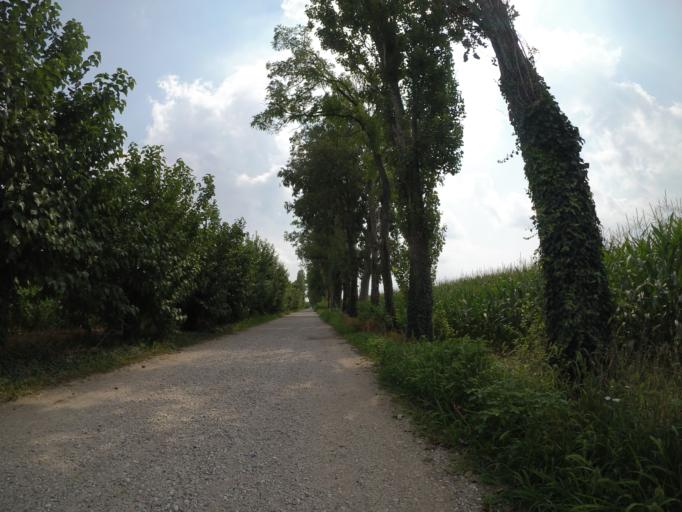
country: IT
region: Friuli Venezia Giulia
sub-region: Provincia di Udine
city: Sedegliano
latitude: 46.0151
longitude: 13.0106
